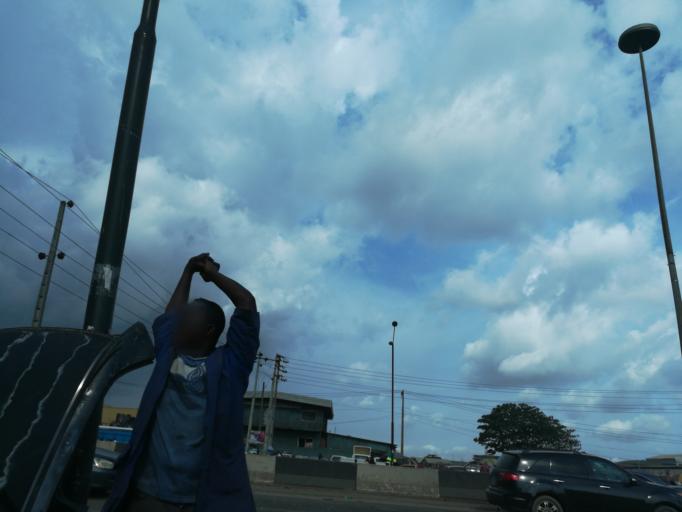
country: NG
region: Lagos
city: Oshodi
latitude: 6.5439
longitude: 3.3373
